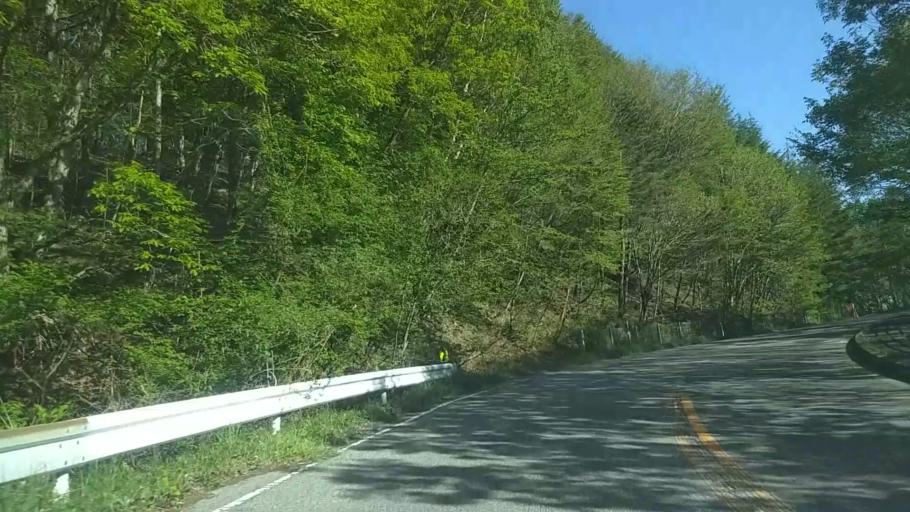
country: JP
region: Yamanashi
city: Nirasaki
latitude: 35.8996
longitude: 138.3654
